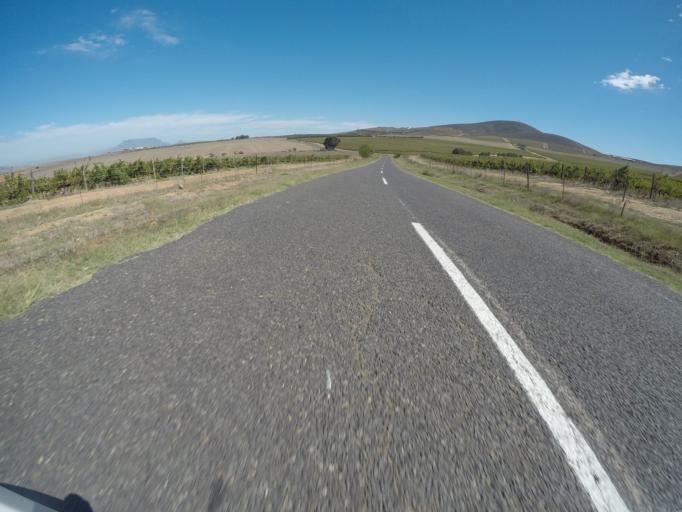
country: ZA
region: Western Cape
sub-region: City of Cape Town
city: Sunset Beach
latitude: -33.7177
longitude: 18.5806
